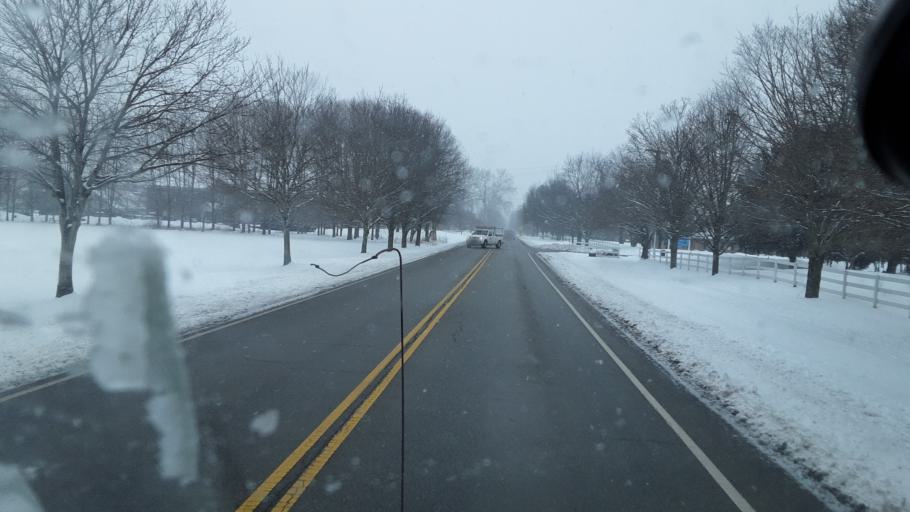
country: US
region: Ohio
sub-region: Licking County
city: Granville
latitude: 40.0601
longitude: -82.4813
